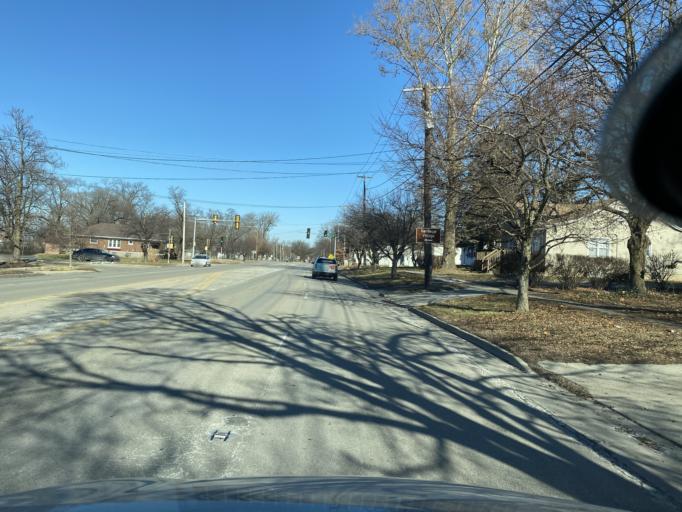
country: US
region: Illinois
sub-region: Will County
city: Lockport
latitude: 41.5959
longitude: -88.0543
